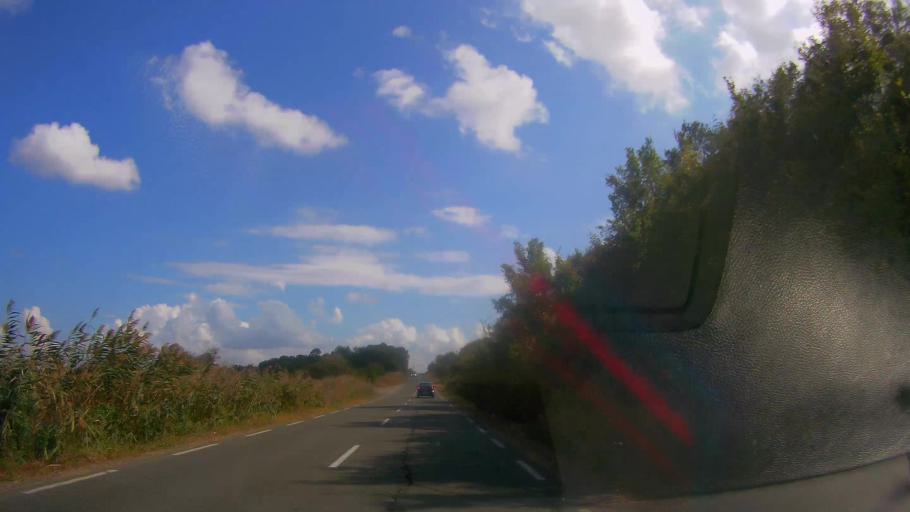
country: BG
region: Burgas
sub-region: Obshtina Kameno
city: Kameno
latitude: 42.4849
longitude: 27.3426
